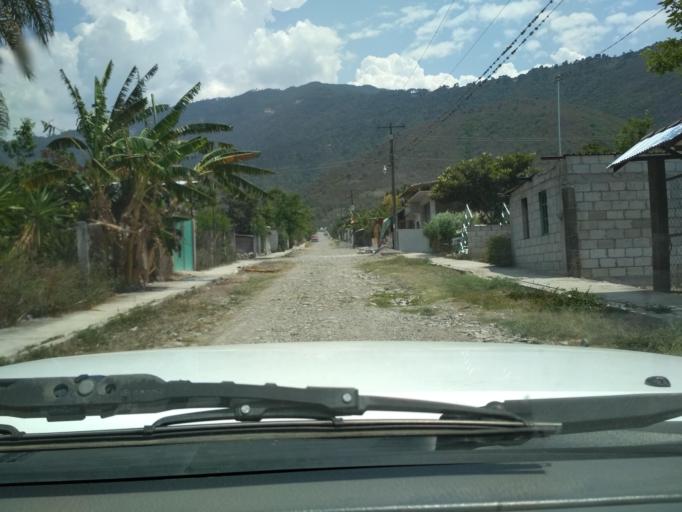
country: MX
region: Veracruz
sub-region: Acultzingo
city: Acatla
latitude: 18.7508
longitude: -97.2202
